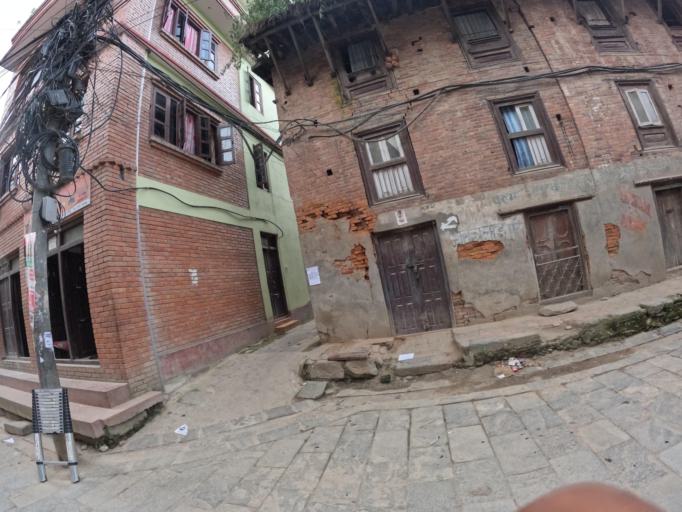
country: NP
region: Central Region
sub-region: Bagmati Zone
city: Bhaktapur
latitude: 27.6813
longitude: 85.3862
